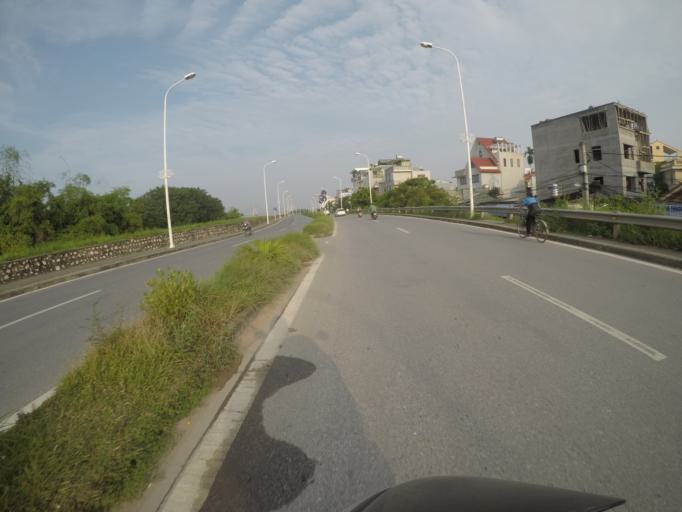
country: VN
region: Ha Noi
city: Tay Ho
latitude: 21.0896
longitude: 105.8021
